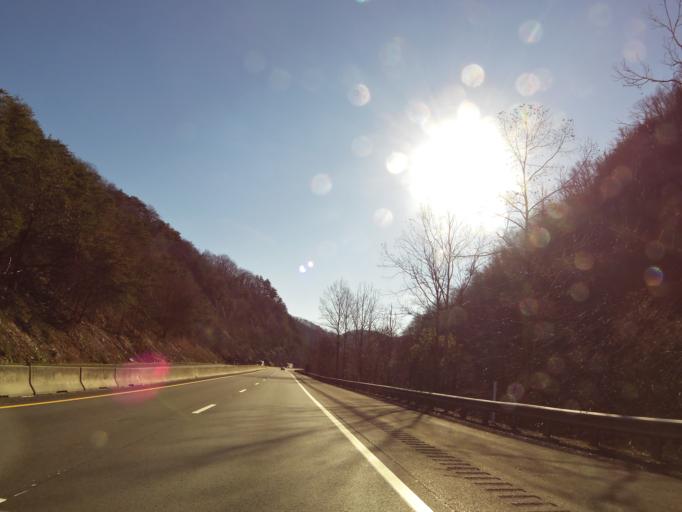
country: US
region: Tennessee
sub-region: Cocke County
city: Newport
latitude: 35.8092
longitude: -83.1418
